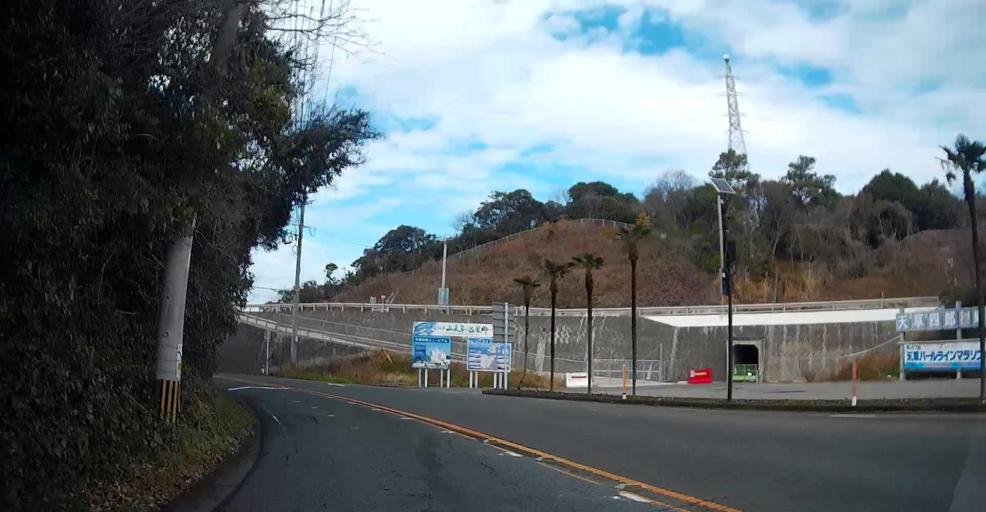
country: JP
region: Kumamoto
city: Yatsushiro
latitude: 32.6131
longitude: 130.4563
